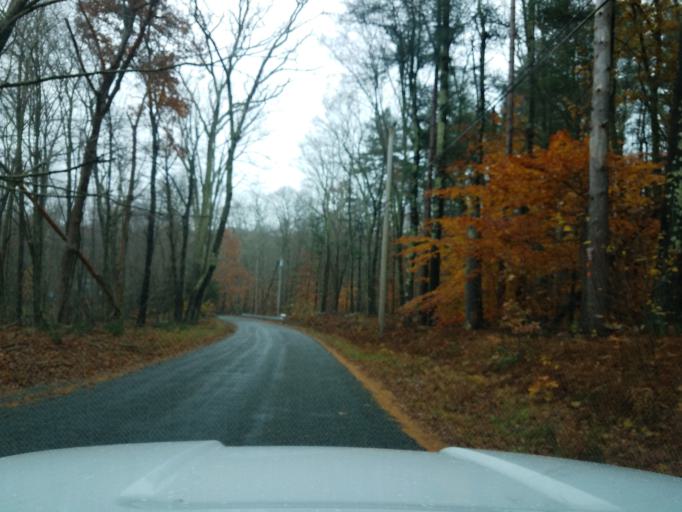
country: US
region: Connecticut
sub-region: Windham County
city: Windham
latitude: 41.7835
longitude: -72.1071
